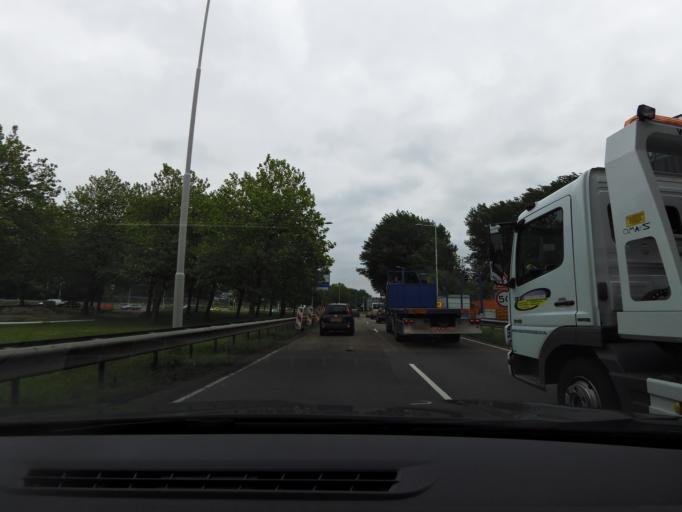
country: NL
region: South Holland
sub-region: Gemeente Albrandswaard
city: Rhoon
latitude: 51.8680
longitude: 4.4458
